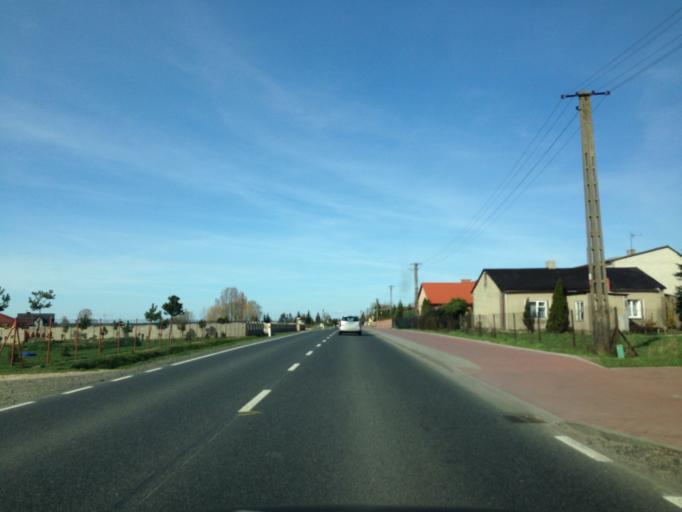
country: PL
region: Lodz Voivodeship
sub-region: Powiat poddebicki
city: Wartkowice
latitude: 51.9785
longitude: 19.0251
